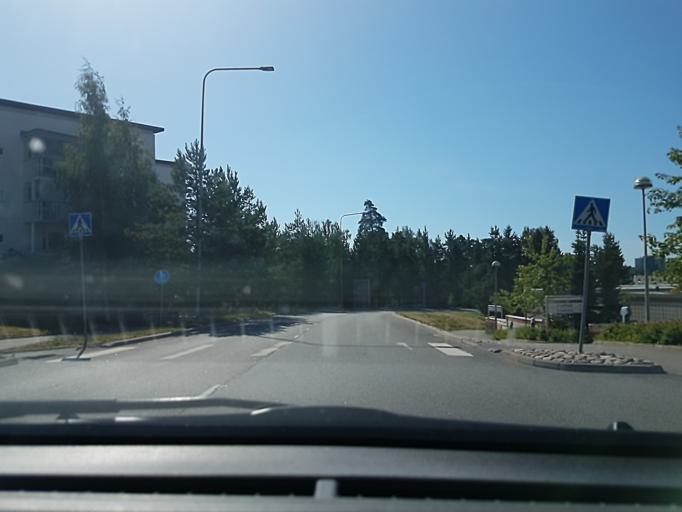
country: FI
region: Uusimaa
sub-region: Helsinki
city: Vantaa
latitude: 60.3317
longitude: 25.0612
